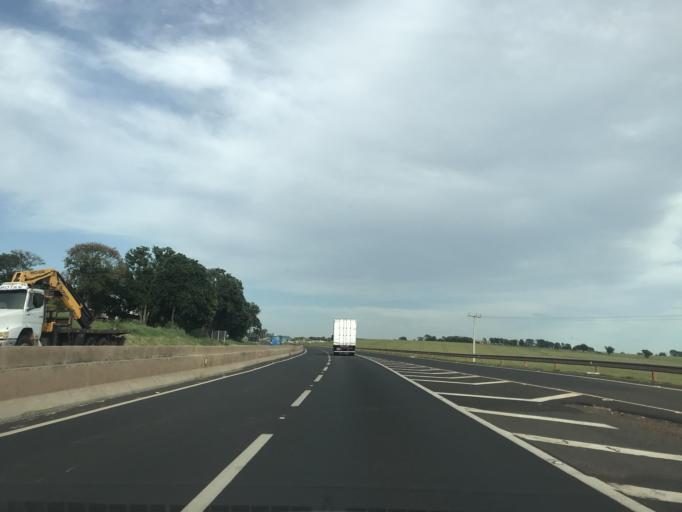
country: BR
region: Parana
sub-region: Mandaguacu
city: Mandaguacu
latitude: -23.3383
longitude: -52.0991
